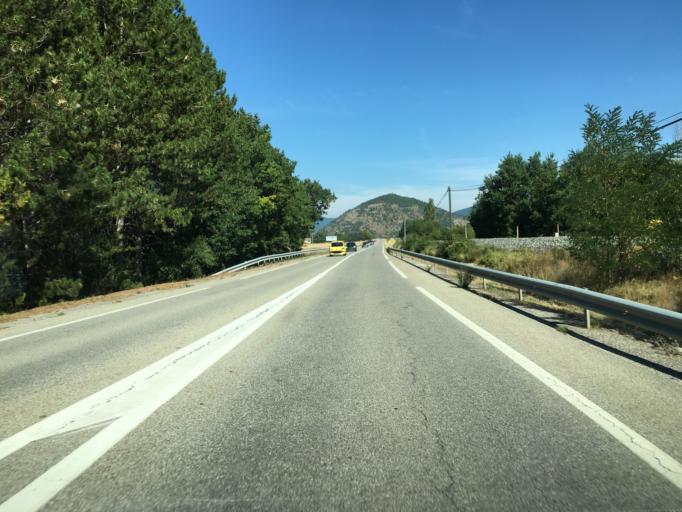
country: FR
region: Provence-Alpes-Cote d'Azur
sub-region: Departement des Hautes-Alpes
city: Laragne-Monteglin
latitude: 44.3610
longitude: 5.7603
